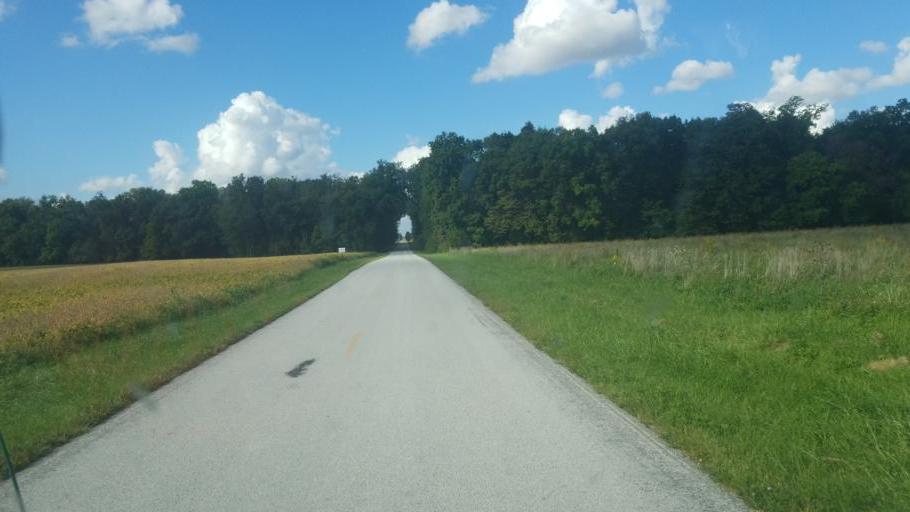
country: US
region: Ohio
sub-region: Hardin County
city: Ada
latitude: 40.7353
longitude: -83.7289
